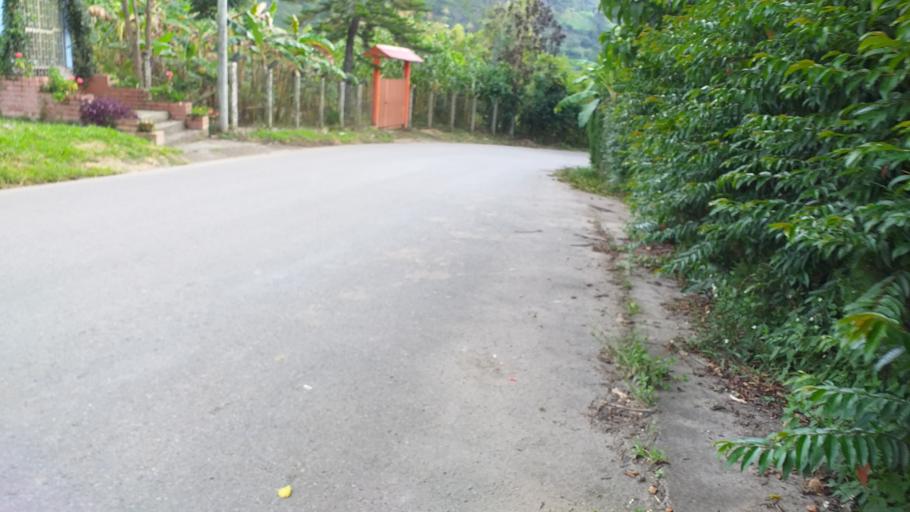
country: CO
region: Cundinamarca
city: Tenza
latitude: 5.0894
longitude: -73.4410
